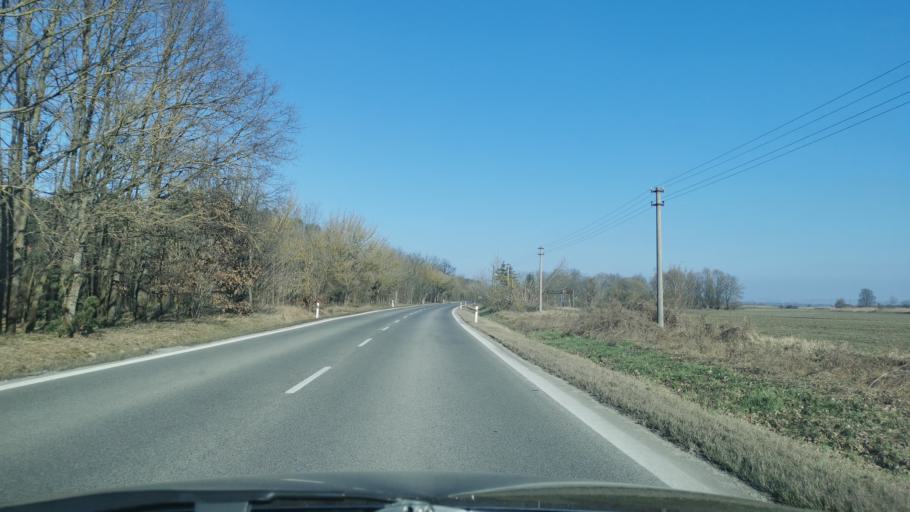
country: SK
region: Trnavsky
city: Gbely
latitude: 48.6694
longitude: 17.2155
